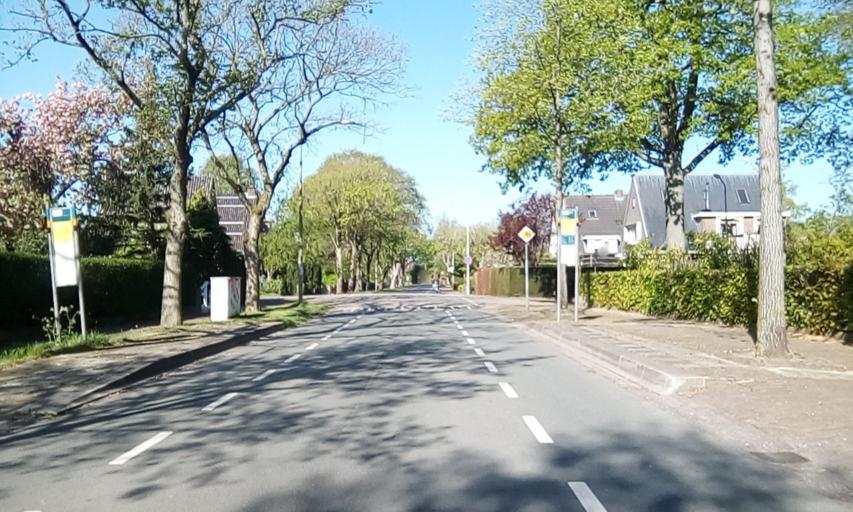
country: NL
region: Gelderland
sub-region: Gemeente Tiel
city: Tiel
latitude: 51.8911
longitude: 5.4202
